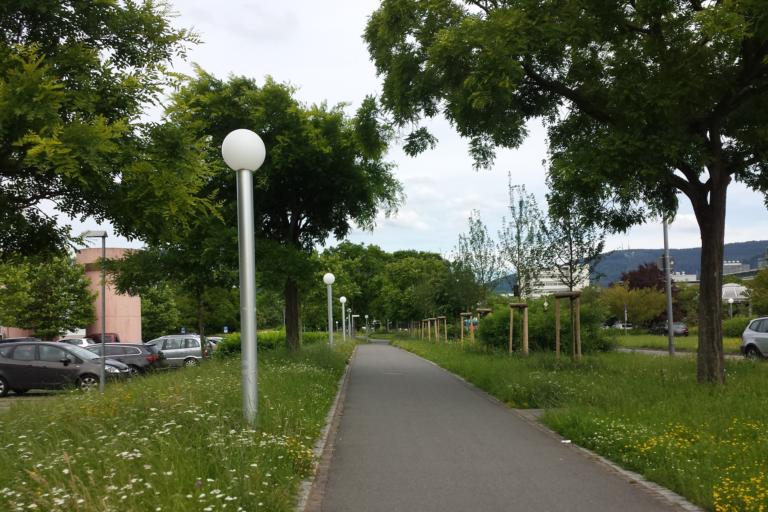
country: DE
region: Baden-Wuerttemberg
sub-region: Karlsruhe Region
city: Heidelberg
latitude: 49.4192
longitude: 8.6650
